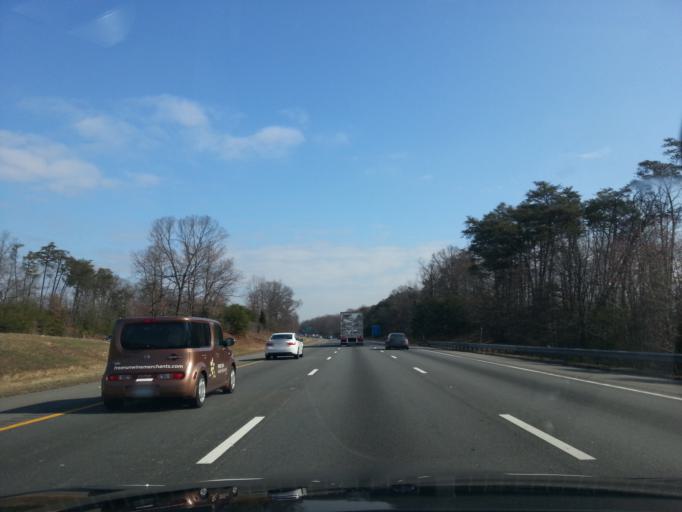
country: US
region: Virginia
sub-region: Stafford County
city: Falmouth
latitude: 38.3577
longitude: -77.4727
